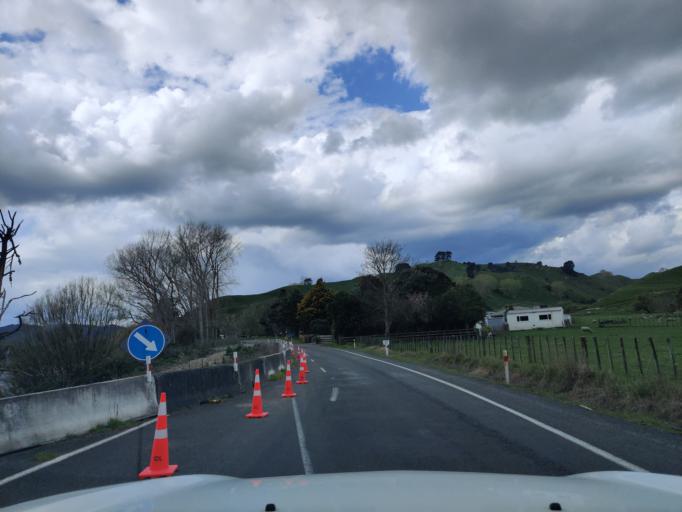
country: NZ
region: Manawatu-Wanganui
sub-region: Wanganui District
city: Wanganui
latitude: -39.8762
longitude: 175.1104
